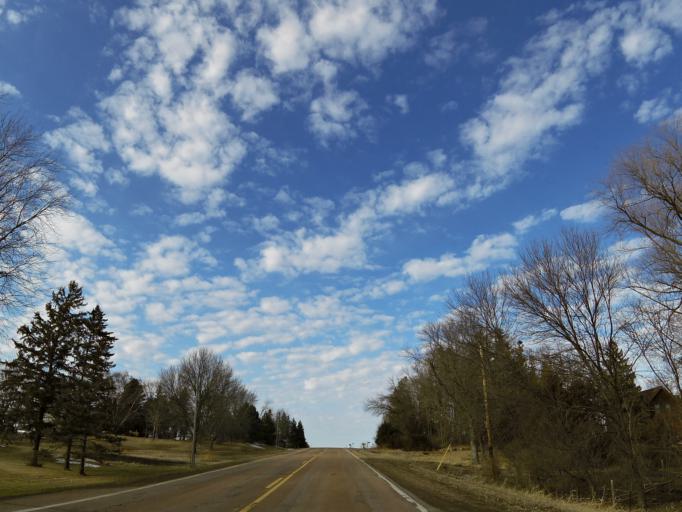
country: US
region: Minnesota
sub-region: Scott County
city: Prior Lake
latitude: 44.6628
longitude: -93.5165
